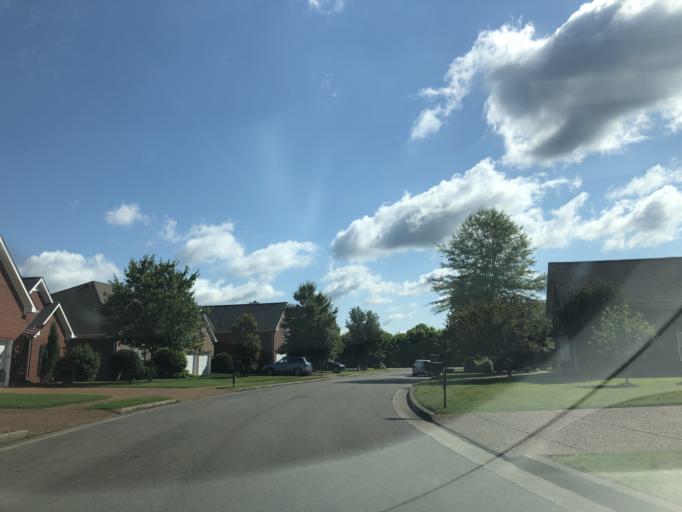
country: US
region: Tennessee
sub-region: Davidson County
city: Belle Meade
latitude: 36.0579
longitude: -86.9482
